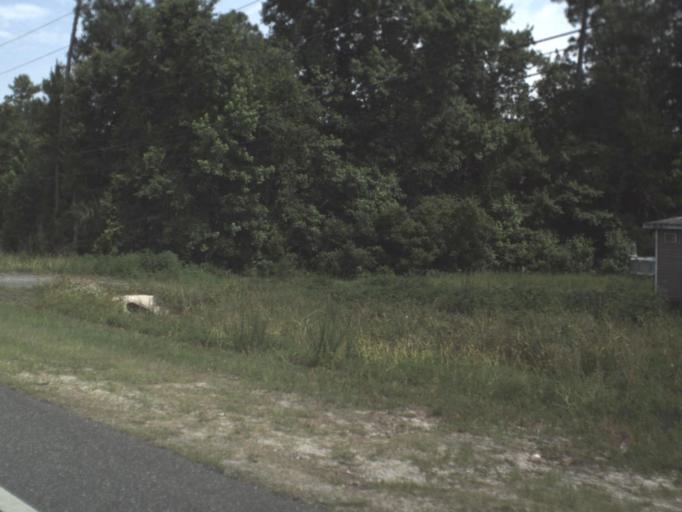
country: US
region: Florida
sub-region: Putnam County
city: Interlachen
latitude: 29.6273
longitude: -81.8016
